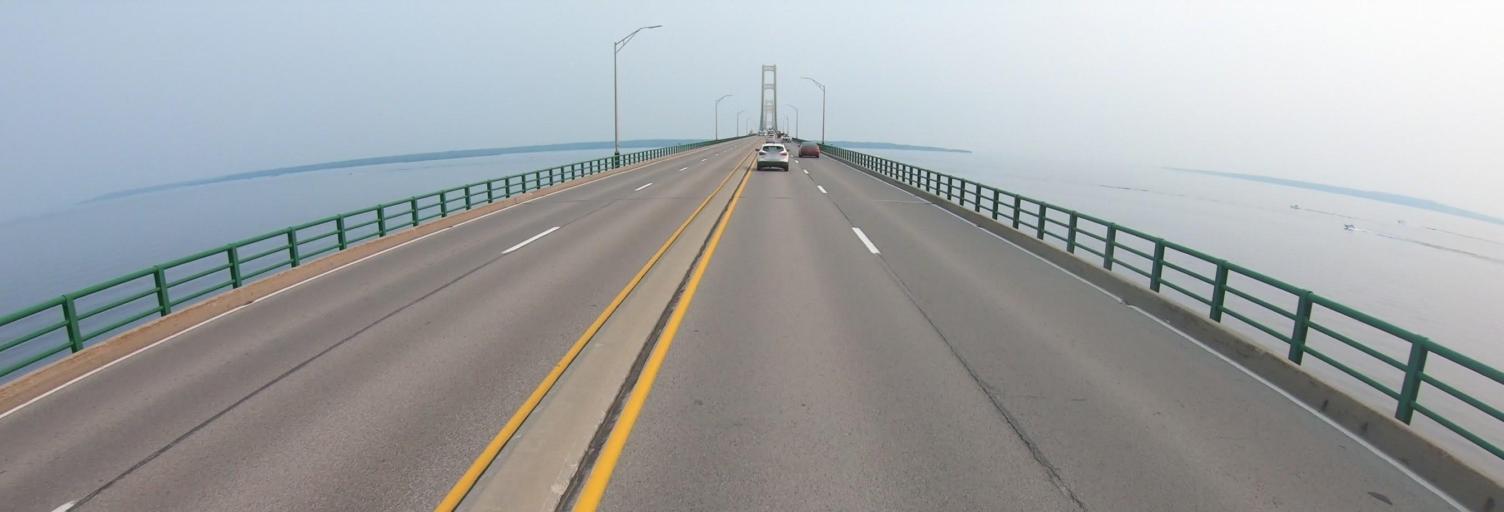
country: US
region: Michigan
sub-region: Mackinac County
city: Saint Ignace
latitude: 45.7982
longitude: -84.7319
